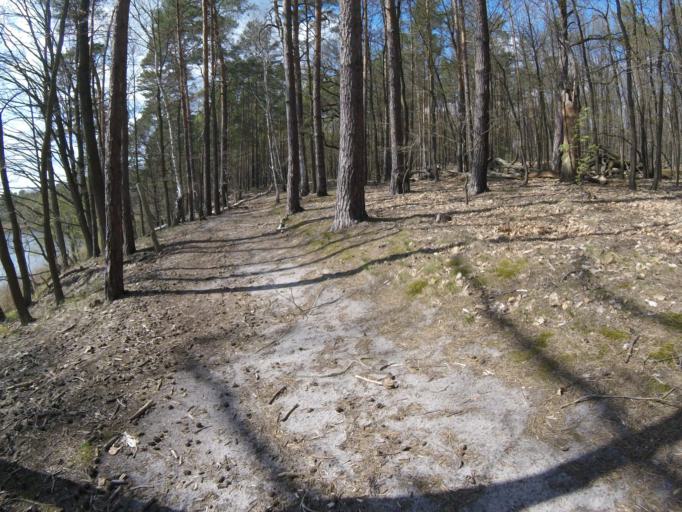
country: DE
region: Brandenburg
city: Gross Koris
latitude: 52.2008
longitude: 13.7169
